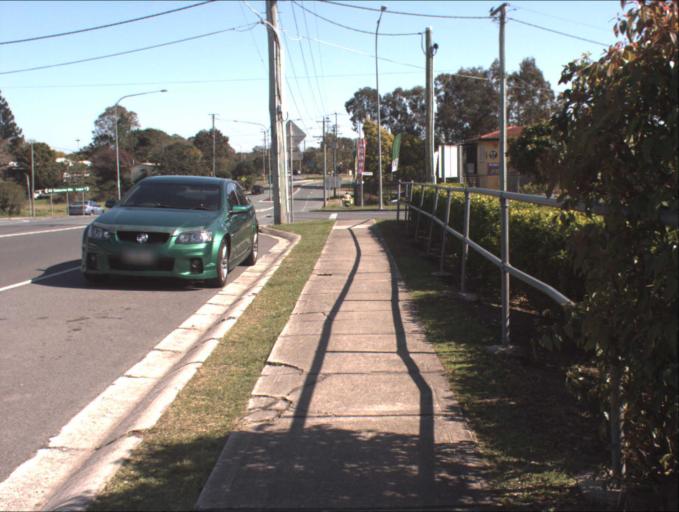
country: AU
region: Queensland
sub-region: Logan
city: Waterford West
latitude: -27.6952
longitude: 153.1433
